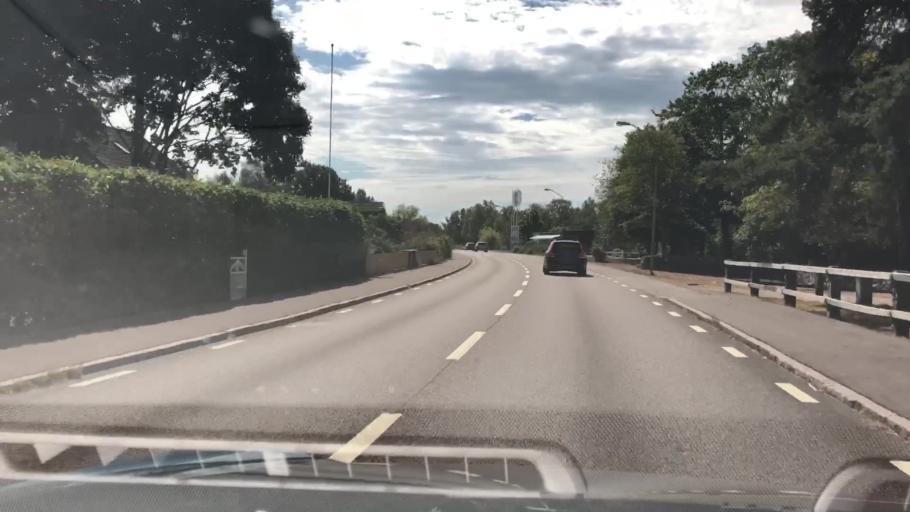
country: SE
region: Kalmar
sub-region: Torsas Kommun
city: Torsas
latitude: 56.3893
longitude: 16.0669
